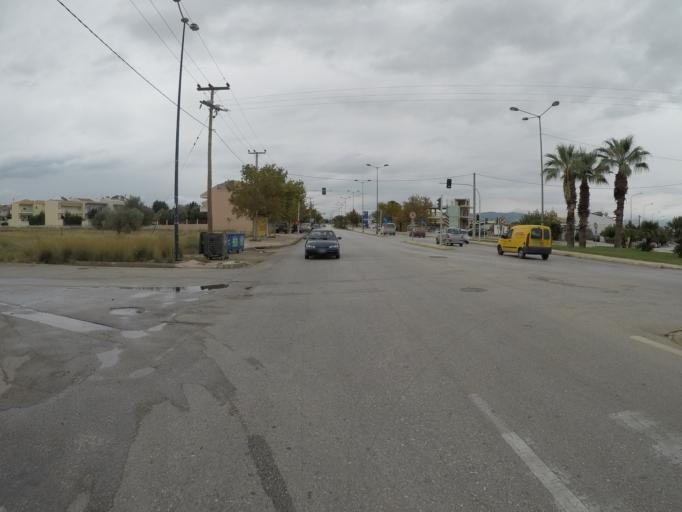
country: GR
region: Peloponnese
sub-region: Nomos Korinthias
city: Loutraki
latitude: 37.9579
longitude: 22.9793
